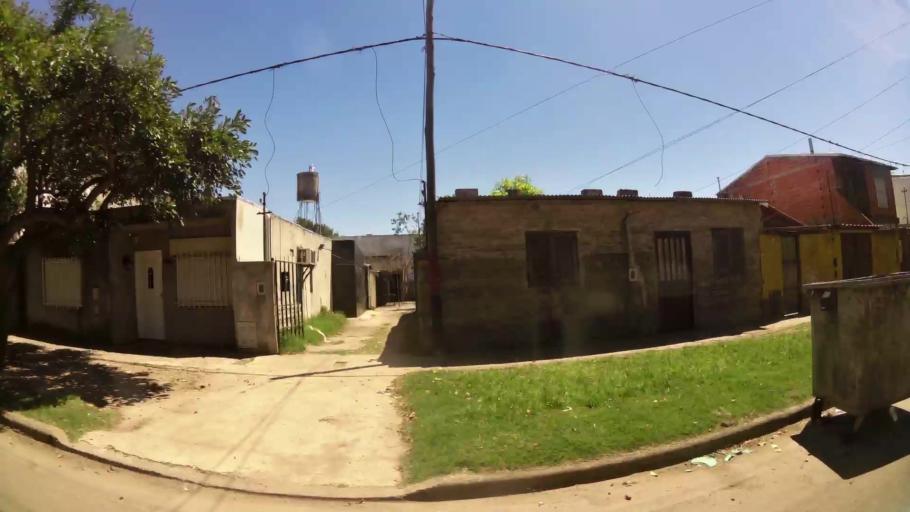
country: AR
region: Santa Fe
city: Perez
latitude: -32.9499
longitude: -60.7186
